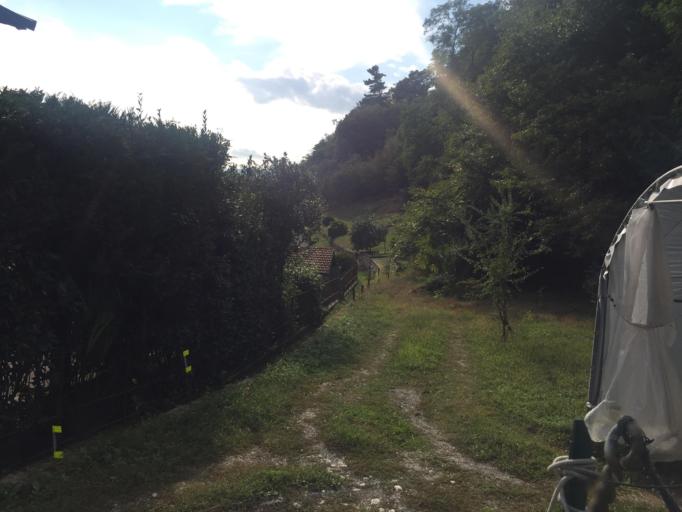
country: IT
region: Piedmont
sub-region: Provincia Verbano-Cusio-Ossola
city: Ghiffa
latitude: 45.9483
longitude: 8.5966
